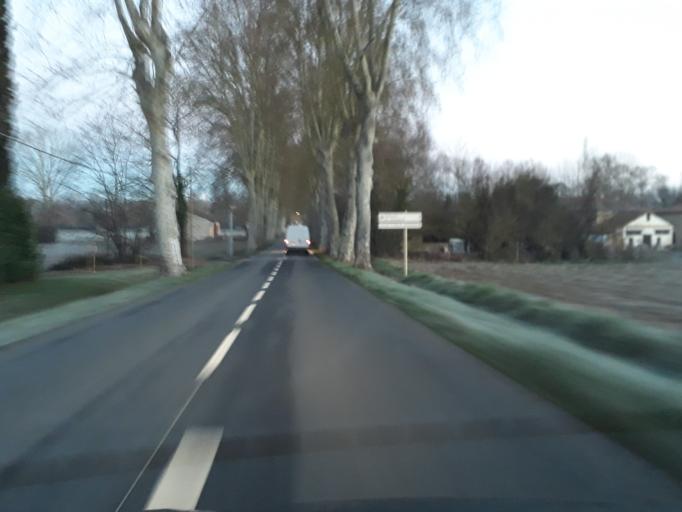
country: FR
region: Midi-Pyrenees
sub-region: Departement du Gers
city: Samatan
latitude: 43.4832
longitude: 0.9365
